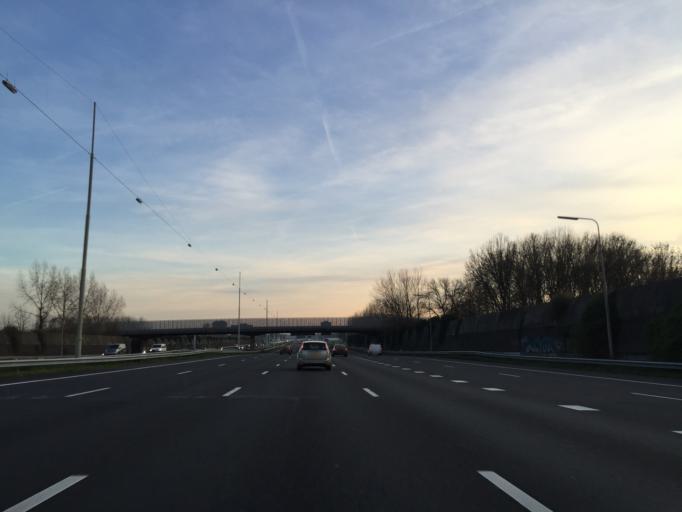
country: NL
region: South Holland
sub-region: Gemeente Ridderkerk
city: Ridderkerk
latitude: 51.8491
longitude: 4.6047
